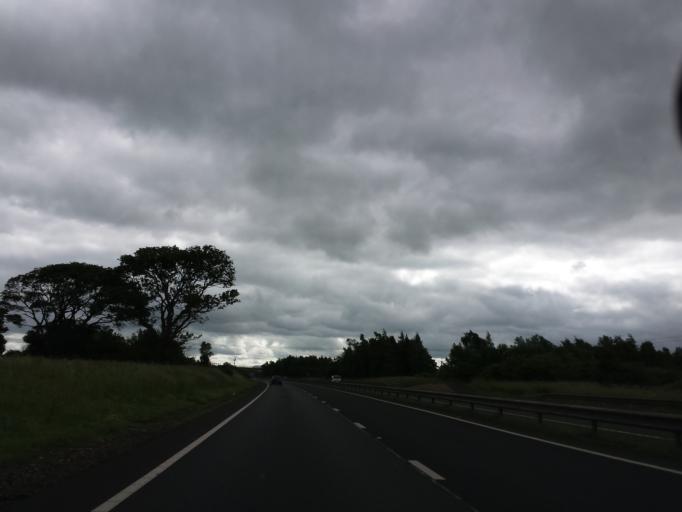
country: GB
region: Scotland
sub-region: East Lothian
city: Macmerry
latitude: 55.9482
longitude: -2.9154
